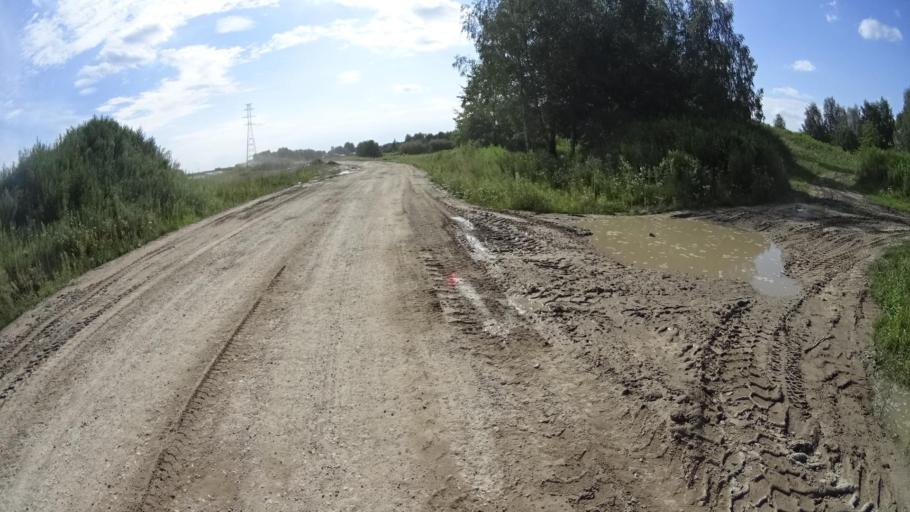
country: PL
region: Masovian Voivodeship
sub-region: Powiat piaseczynski
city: Lesznowola
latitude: 52.0622
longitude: 20.9365
